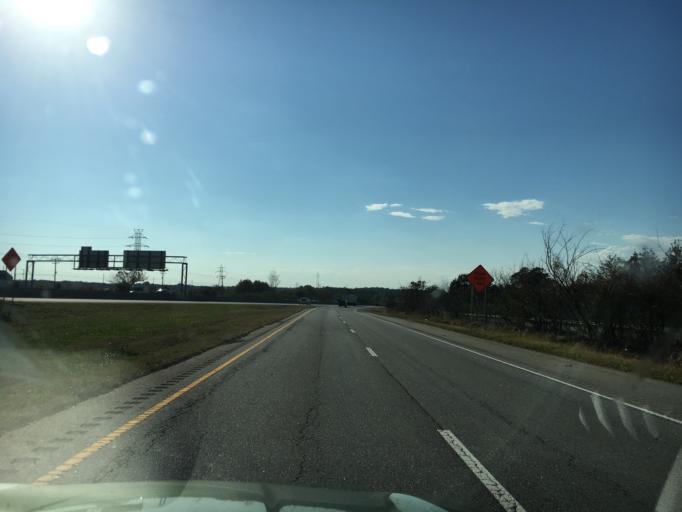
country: US
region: South Carolina
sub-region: Spartanburg County
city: Fairforest
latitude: 34.9642
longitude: -82.0368
